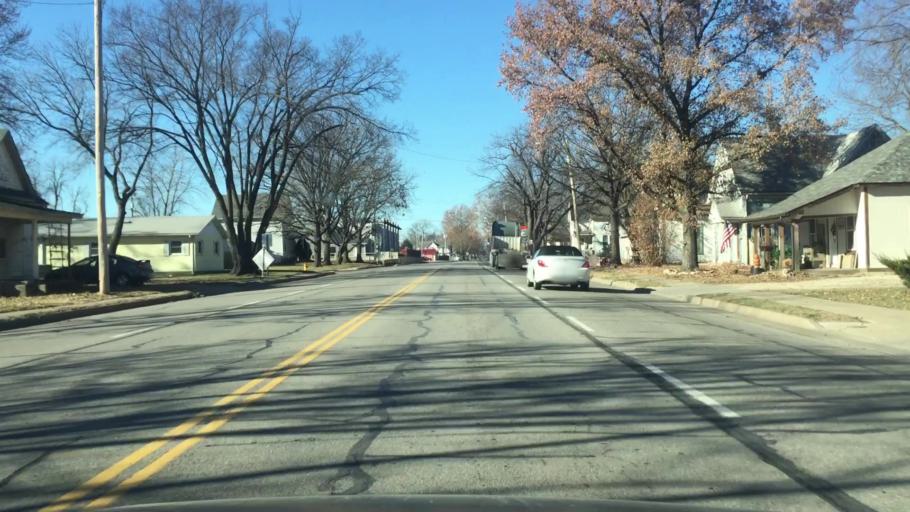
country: US
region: Kansas
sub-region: Allen County
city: Iola
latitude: 37.9221
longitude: -95.3920
